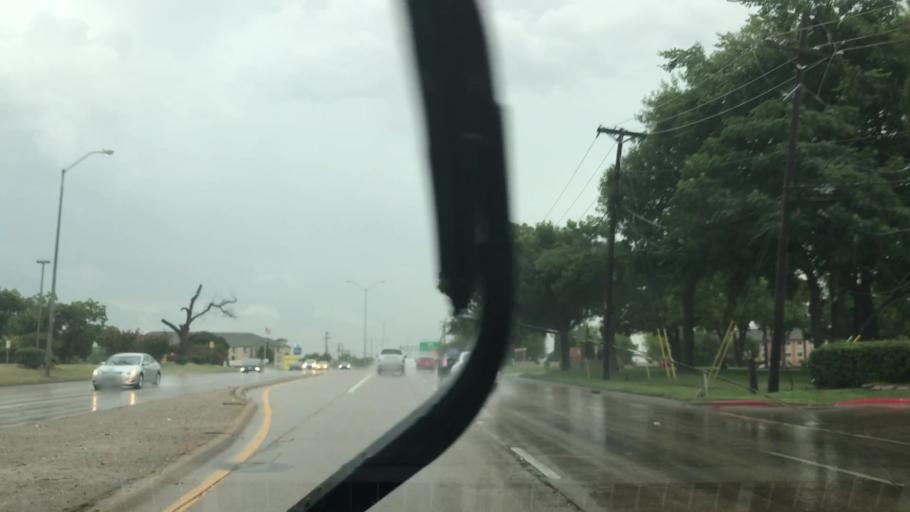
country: US
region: Texas
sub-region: Dallas County
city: Farmers Branch
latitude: 32.8606
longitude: -96.8883
